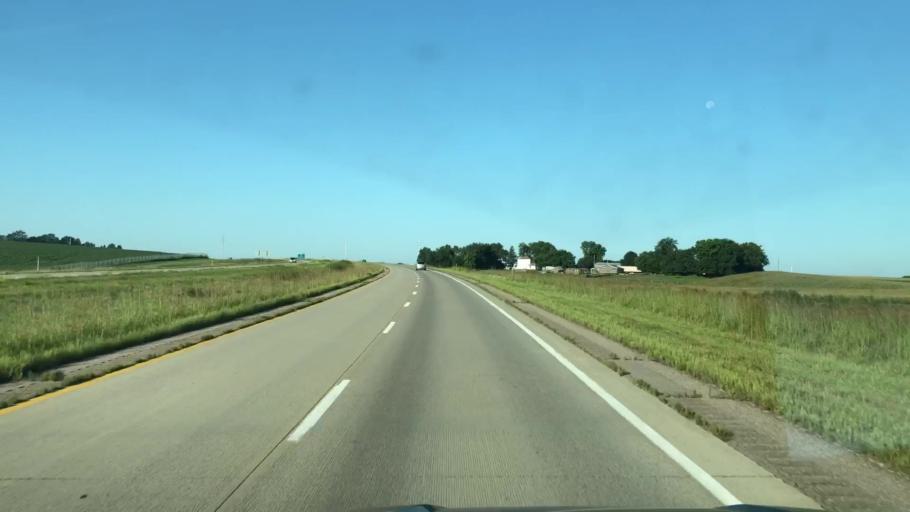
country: US
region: Iowa
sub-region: Plymouth County
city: Le Mars
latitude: 42.8157
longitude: -96.1879
